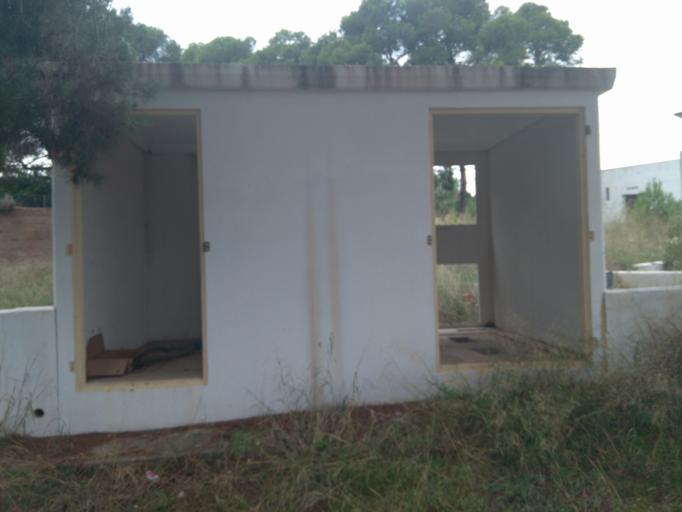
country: ES
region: Valencia
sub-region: Provincia de Valencia
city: Benimodo
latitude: 39.1936
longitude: -0.5687
